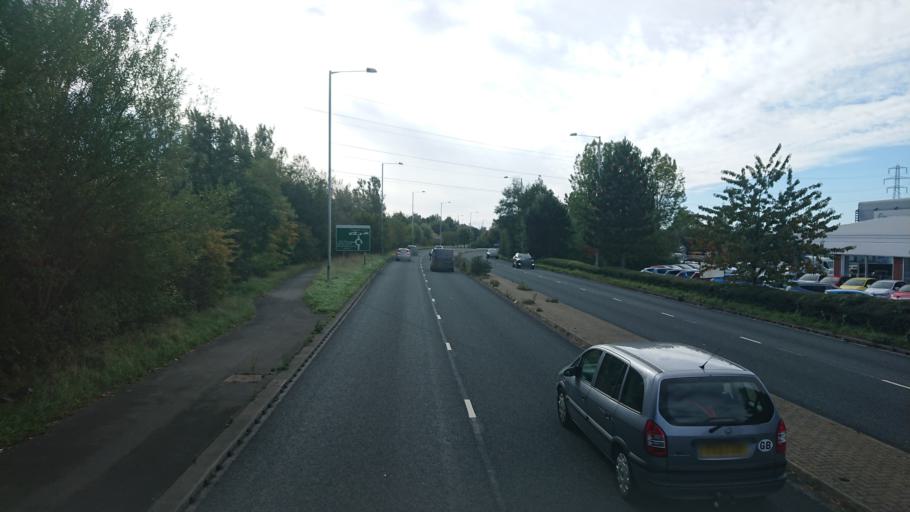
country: GB
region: England
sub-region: Lancashire
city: Morecambe
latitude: 54.0561
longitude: -2.8373
